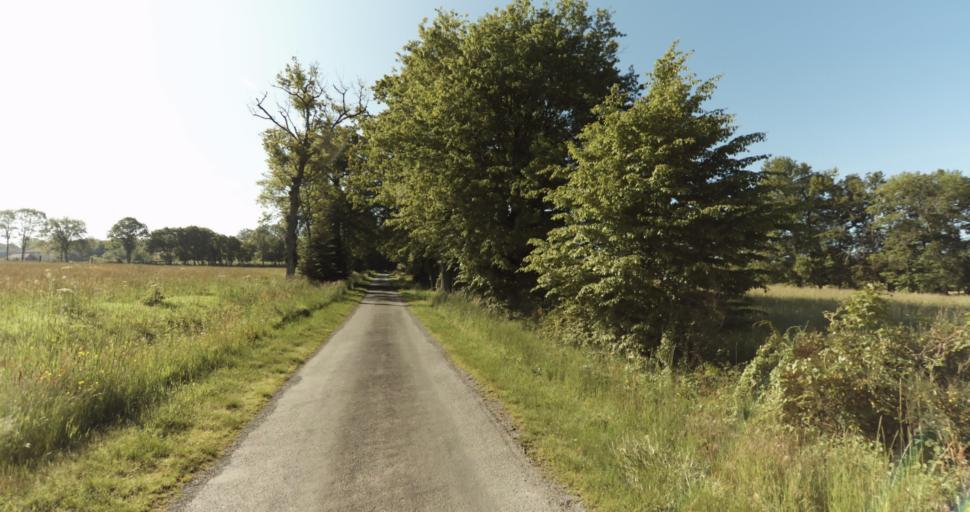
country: FR
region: Limousin
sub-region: Departement de la Haute-Vienne
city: Bosmie-l'Aiguille
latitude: 45.7268
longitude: 1.2373
